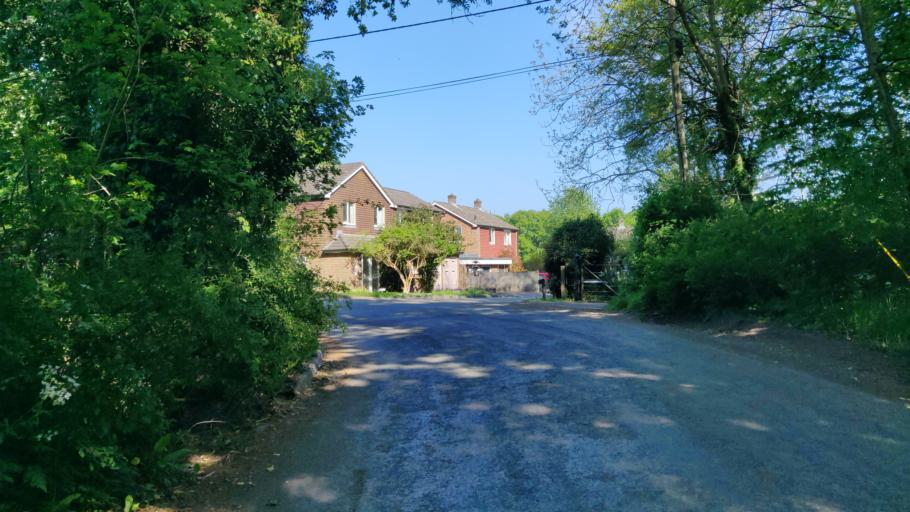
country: GB
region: England
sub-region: West Sussex
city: Billingshurst
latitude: 51.0251
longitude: -0.4105
